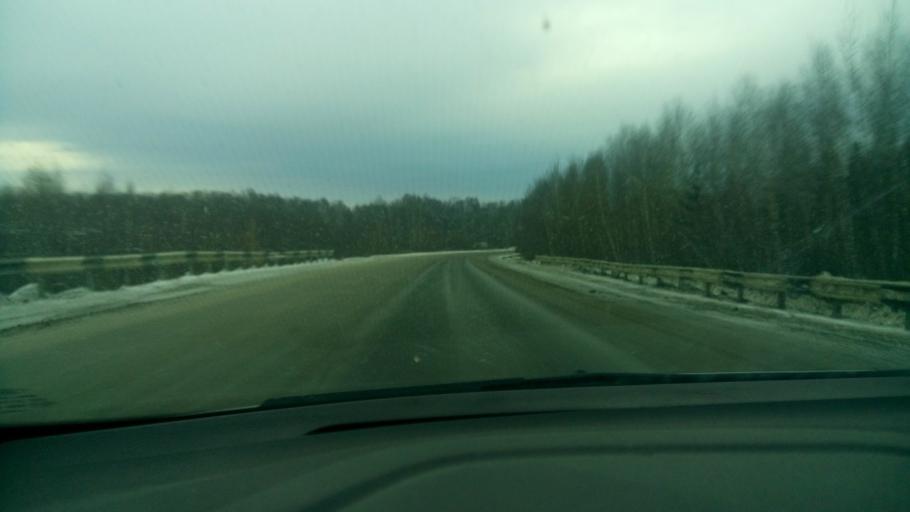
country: RU
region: Sverdlovsk
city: Istok
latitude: 56.7605
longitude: 60.7641
